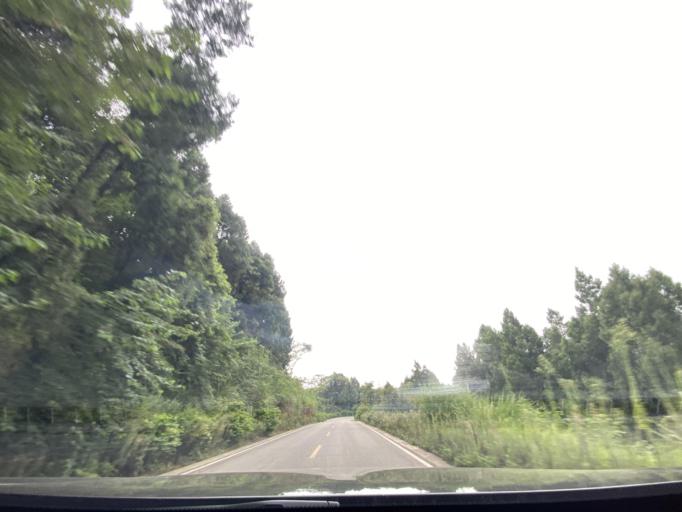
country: CN
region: Sichuan
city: Jiancheng
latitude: 30.5351
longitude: 104.5336
